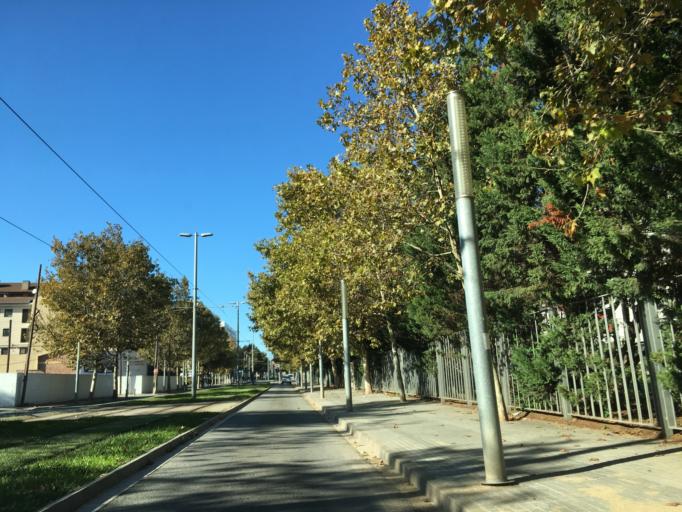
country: ES
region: Catalonia
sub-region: Provincia de Barcelona
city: Sant Joan Despi
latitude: 41.3591
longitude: 2.0637
